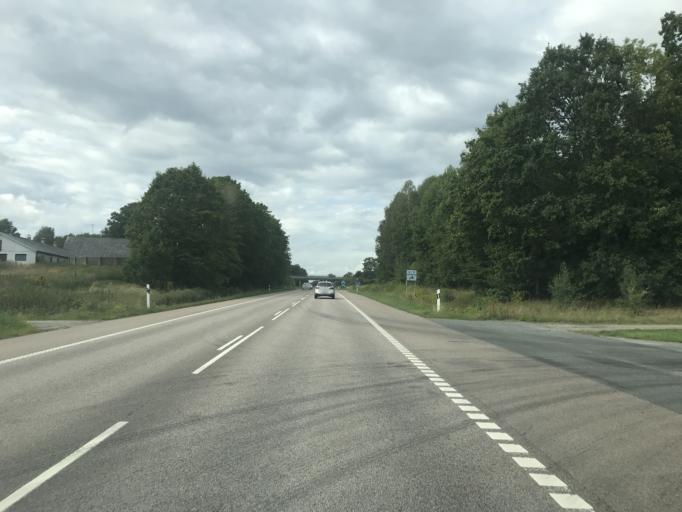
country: SE
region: Skane
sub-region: Hassleholms Kommun
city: Hassleholm
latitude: 56.1385
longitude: 13.8062
